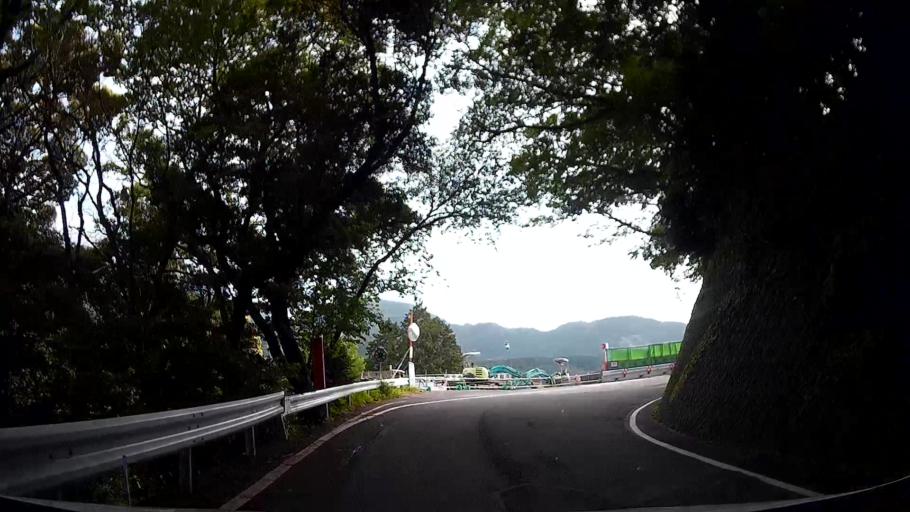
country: JP
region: Shizuoka
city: Heda
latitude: 34.9095
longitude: 138.8198
